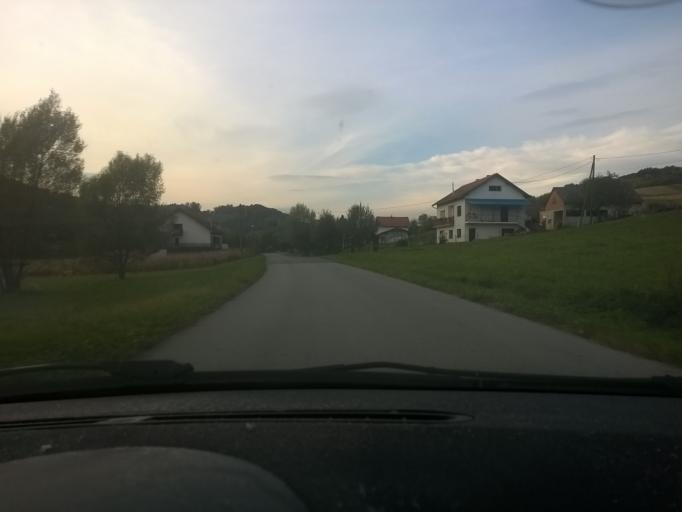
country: HR
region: Krapinsko-Zagorska
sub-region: Grad Krapina
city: Krapina
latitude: 46.1120
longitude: 15.8667
